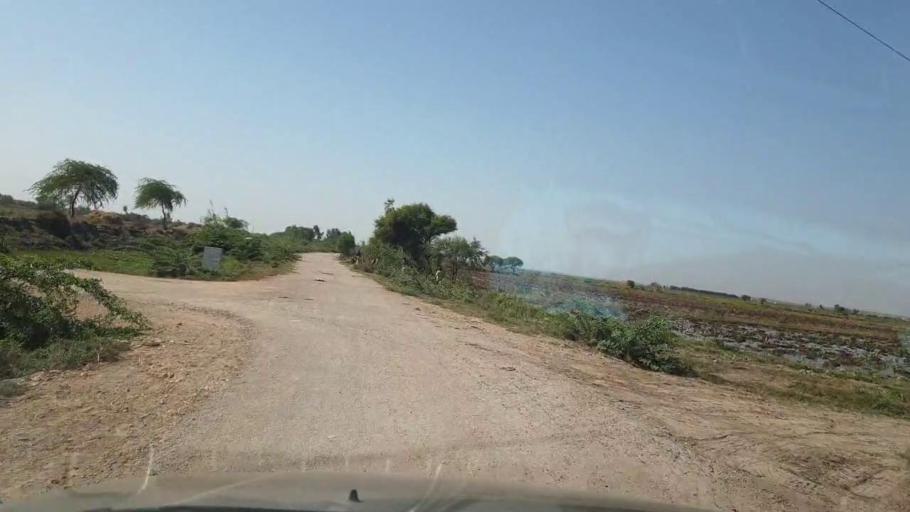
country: PK
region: Sindh
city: Thatta
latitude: 24.7235
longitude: 67.9234
